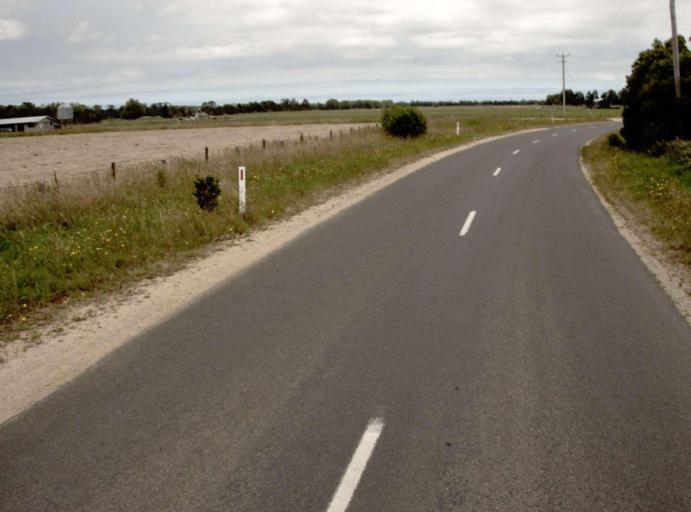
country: AU
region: Victoria
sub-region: Latrobe
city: Traralgon
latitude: -38.4956
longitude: 146.6789
